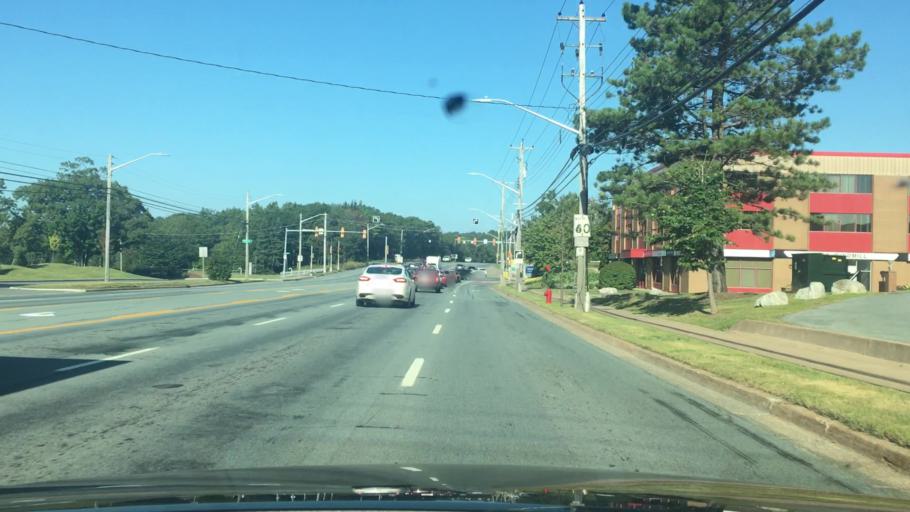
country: CA
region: Nova Scotia
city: Dartmouth
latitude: 44.7030
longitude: -63.6102
